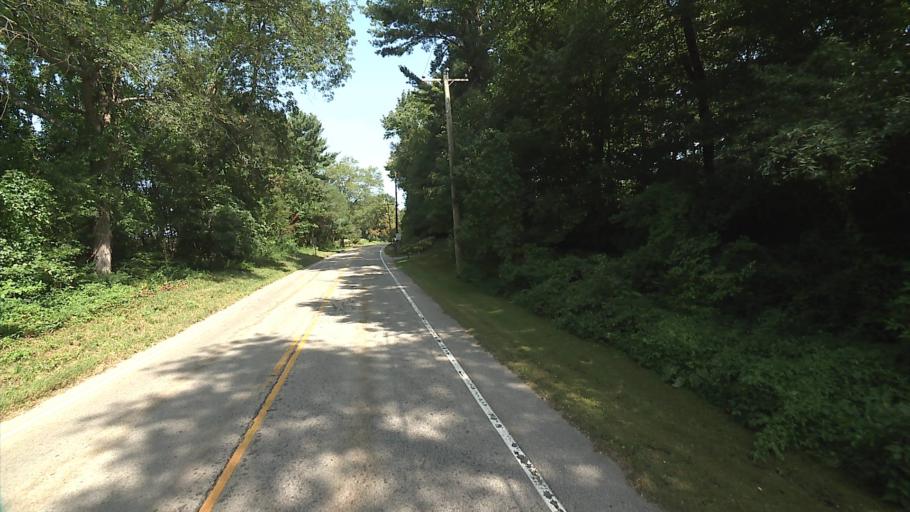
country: US
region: Connecticut
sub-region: Windham County
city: South Woodstock
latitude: 41.9215
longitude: -71.9568
